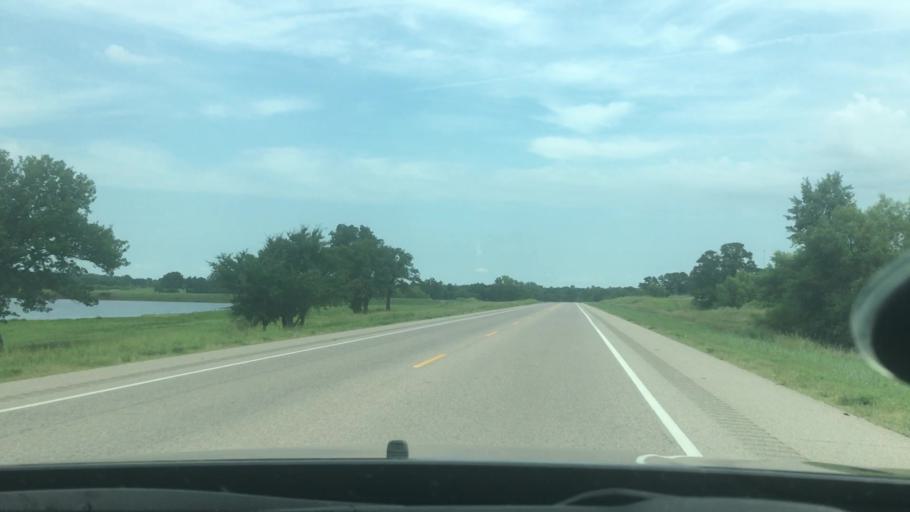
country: US
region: Oklahoma
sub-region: Seminole County
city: Seminole
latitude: 35.1676
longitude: -96.6742
